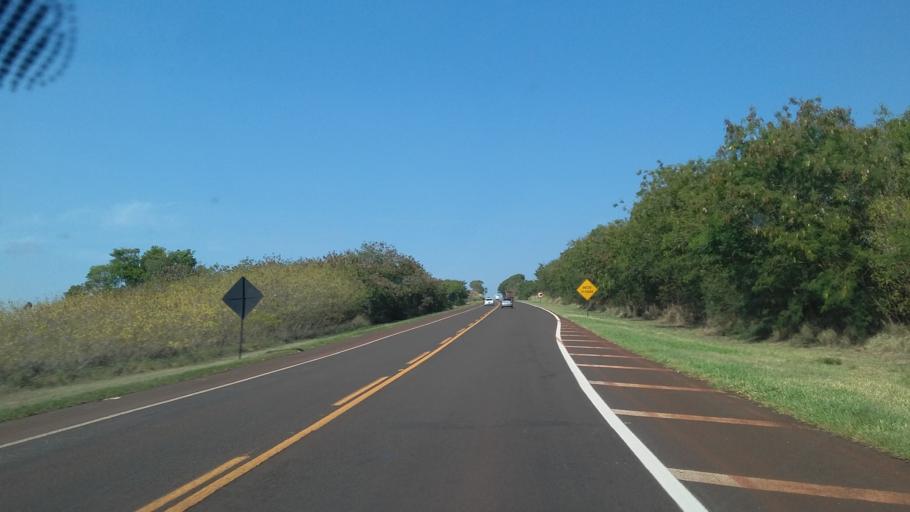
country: BR
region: Parana
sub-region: Bandeirantes
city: Bandeirantes
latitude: -23.1184
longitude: -50.3465
